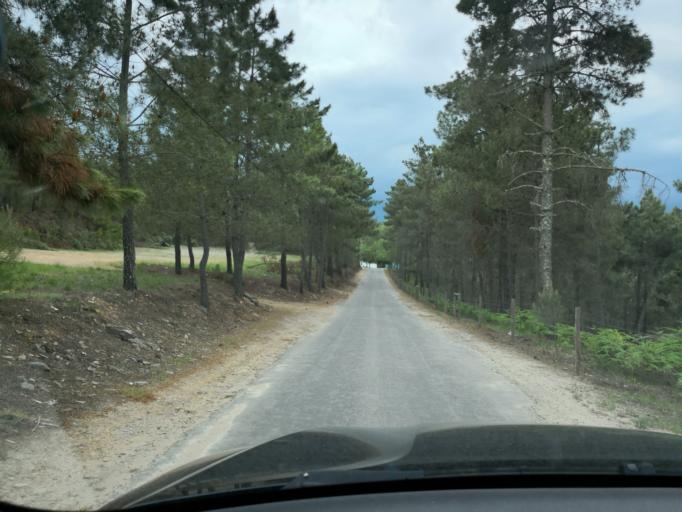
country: PT
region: Vila Real
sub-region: Sabrosa
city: Vilela
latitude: 41.2305
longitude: -7.6714
